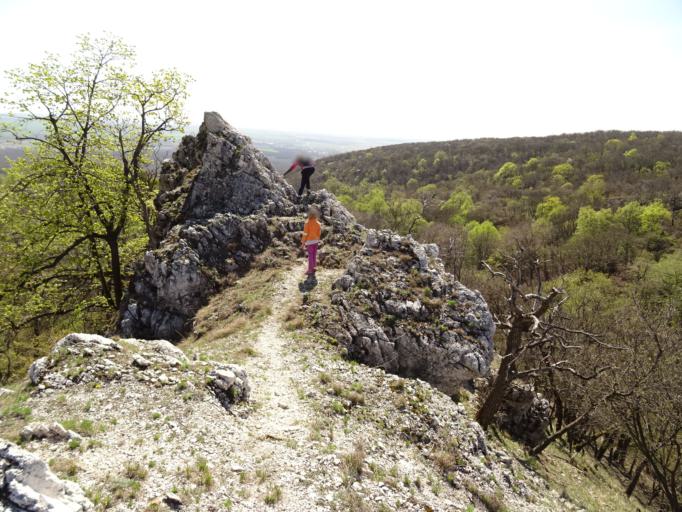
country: HU
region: Fejer
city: Csakvar
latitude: 47.4316
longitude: 18.4388
